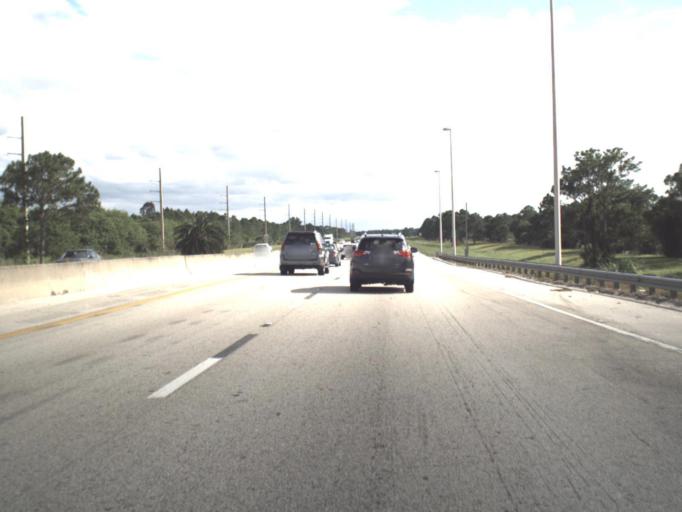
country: US
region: Florida
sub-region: Martin County
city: North River Shores
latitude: 27.2048
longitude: -80.3315
